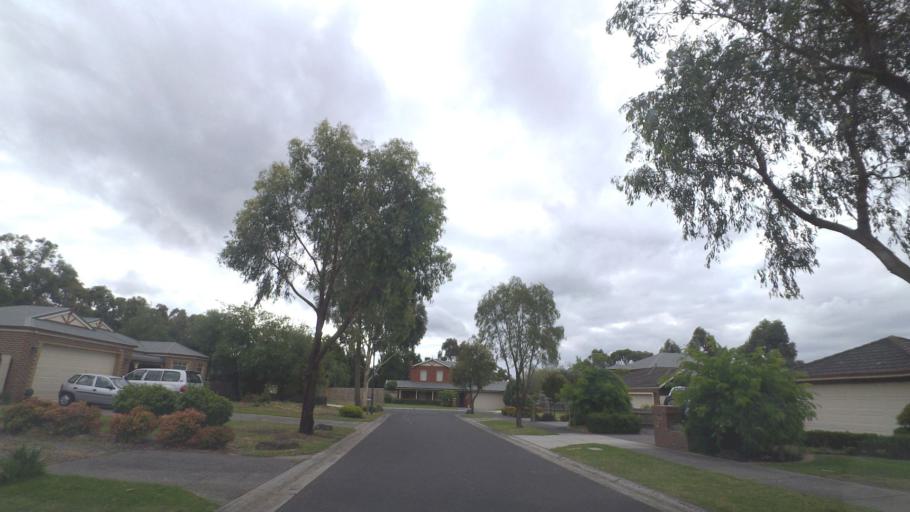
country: AU
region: Victoria
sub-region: Maroondah
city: Kilsyth South
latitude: -37.8226
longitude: 145.3103
